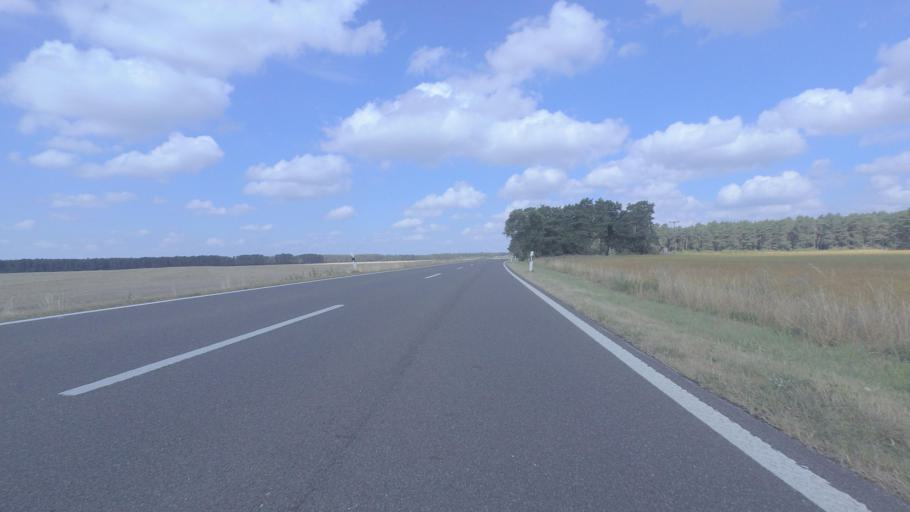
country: DE
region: Brandenburg
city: Walsleben
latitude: 53.0224
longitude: 12.6276
